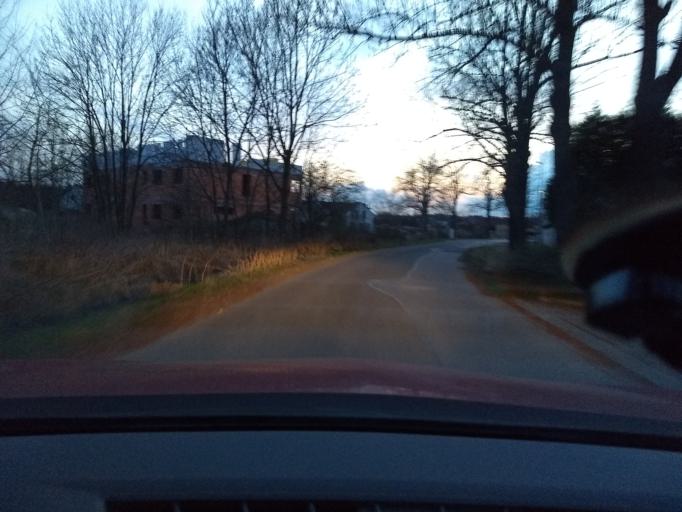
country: CZ
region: Central Bohemia
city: Jenec
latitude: 50.0508
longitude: 14.1807
